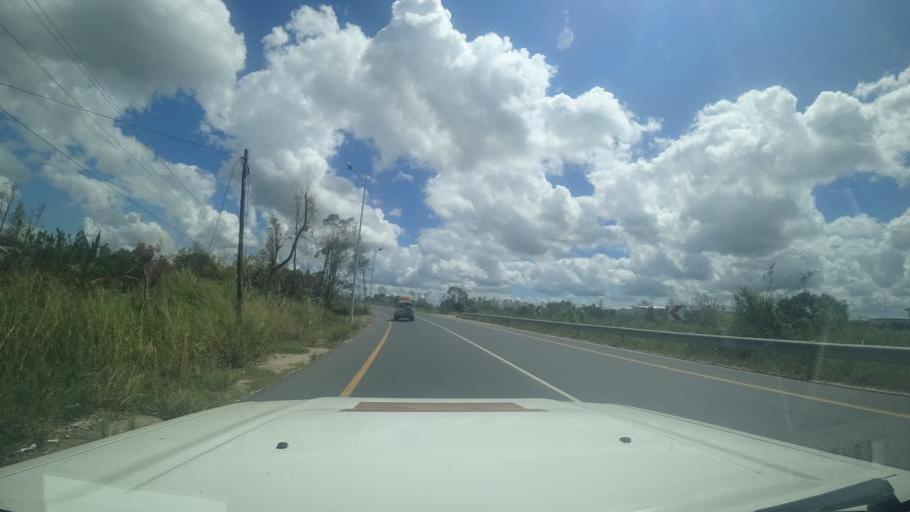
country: MZ
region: Sofala
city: Dondo
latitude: -19.5728
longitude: 34.7162
